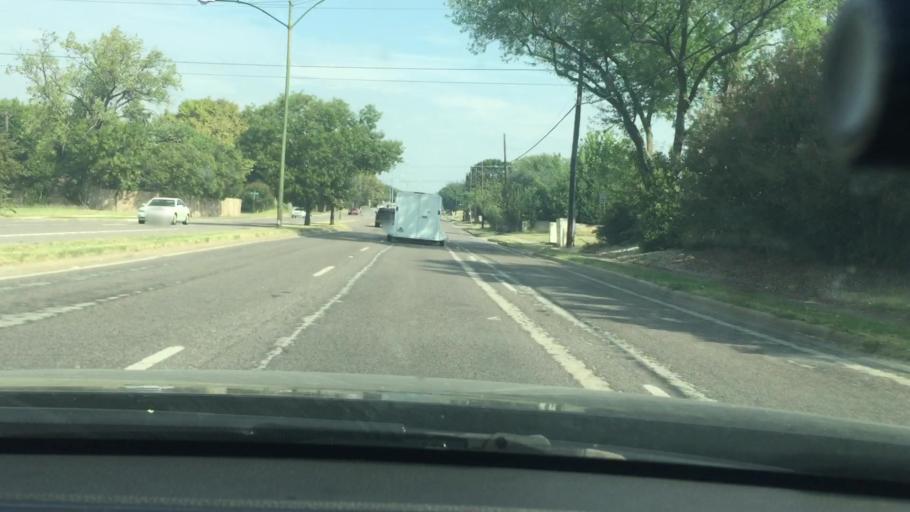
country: US
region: Texas
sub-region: Dallas County
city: Farmers Branch
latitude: 32.8993
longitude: -96.8561
